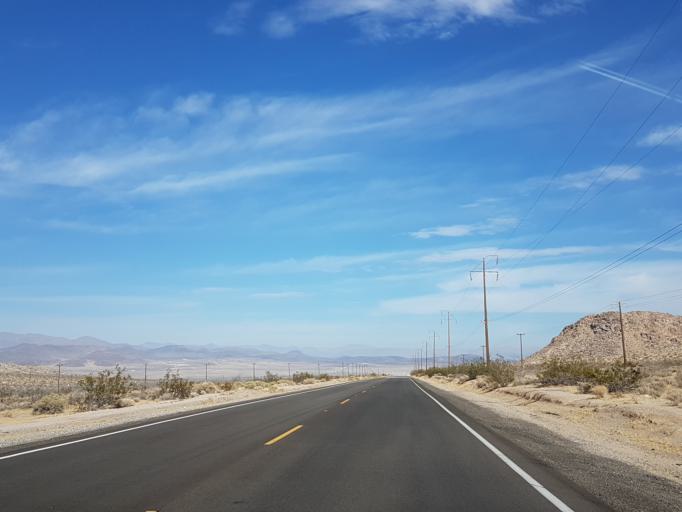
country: US
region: California
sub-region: Kern County
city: Ridgecrest
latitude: 35.6316
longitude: -117.5806
